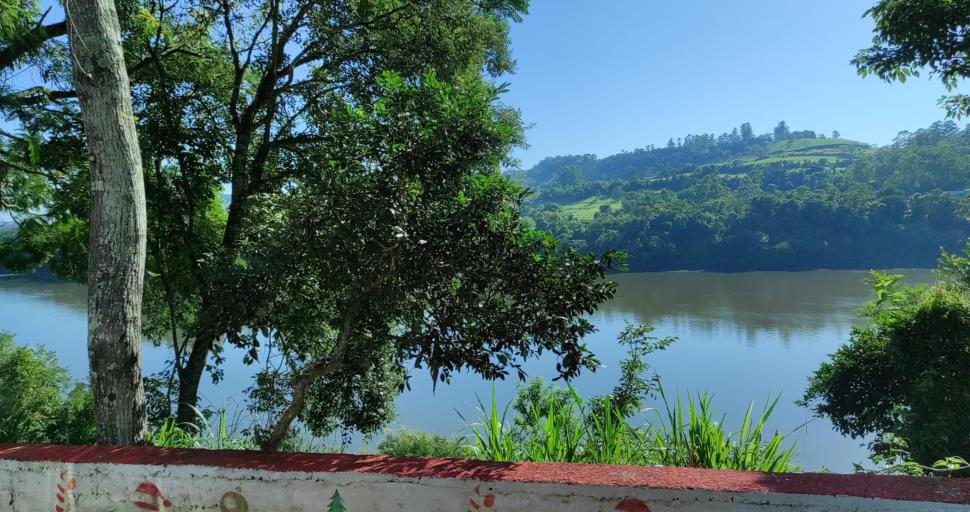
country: AR
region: Misiones
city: El Soberbio
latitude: -27.2962
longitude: -54.1944
